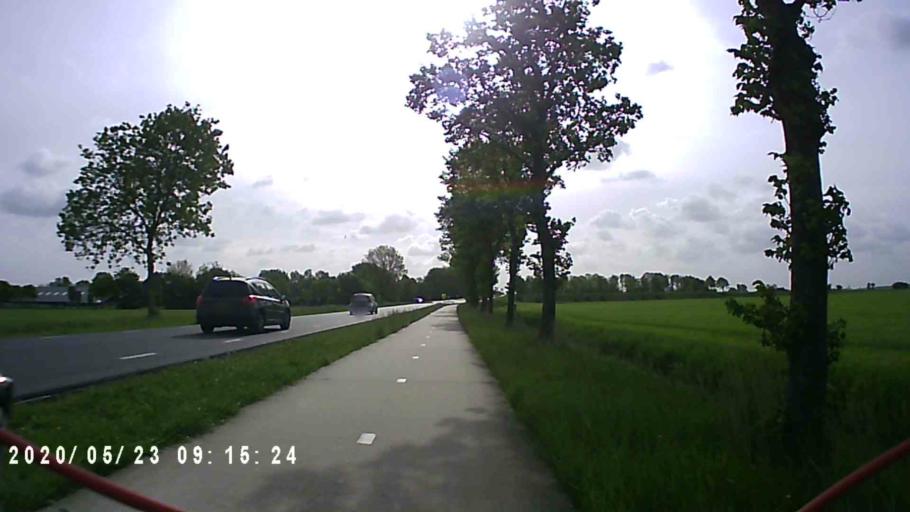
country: NL
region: Groningen
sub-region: Gemeente Bedum
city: Bedum
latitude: 53.3025
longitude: 6.6432
